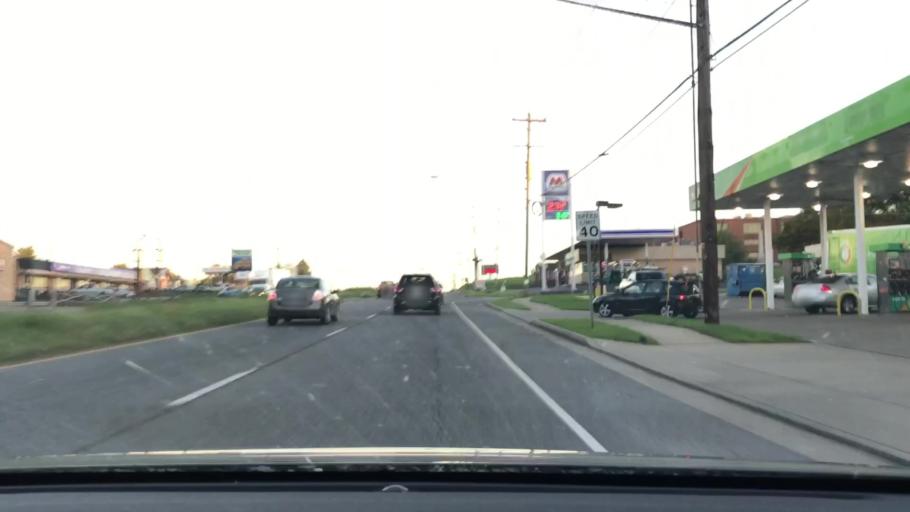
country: US
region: Tennessee
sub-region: Williamson County
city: Brentwood
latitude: 36.0595
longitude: -86.7162
